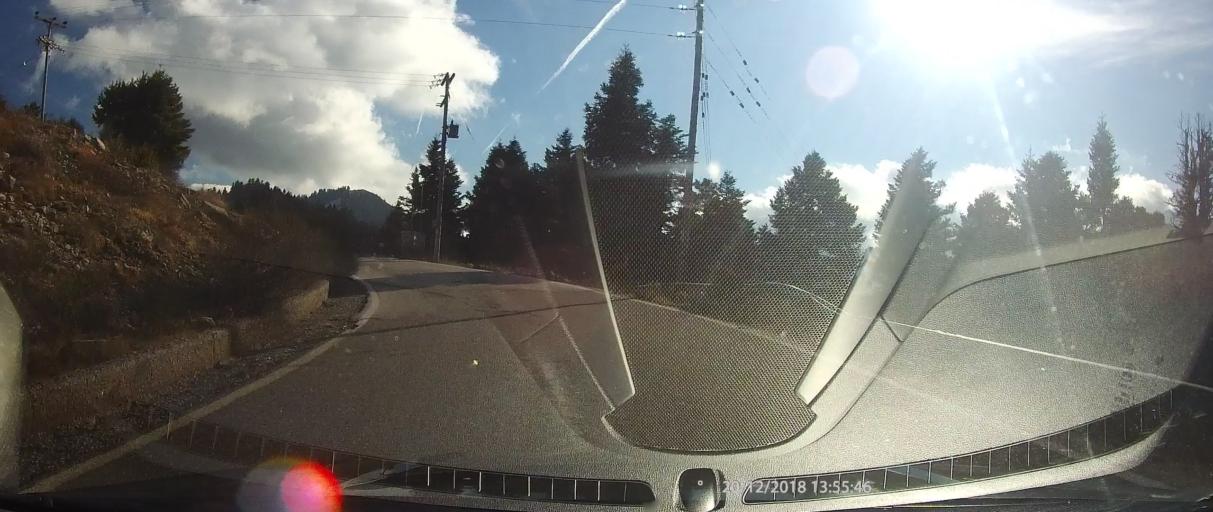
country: GR
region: West Greece
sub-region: Nomos Aitolias kai Akarnanias
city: Paravola
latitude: 38.7085
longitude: 21.6132
